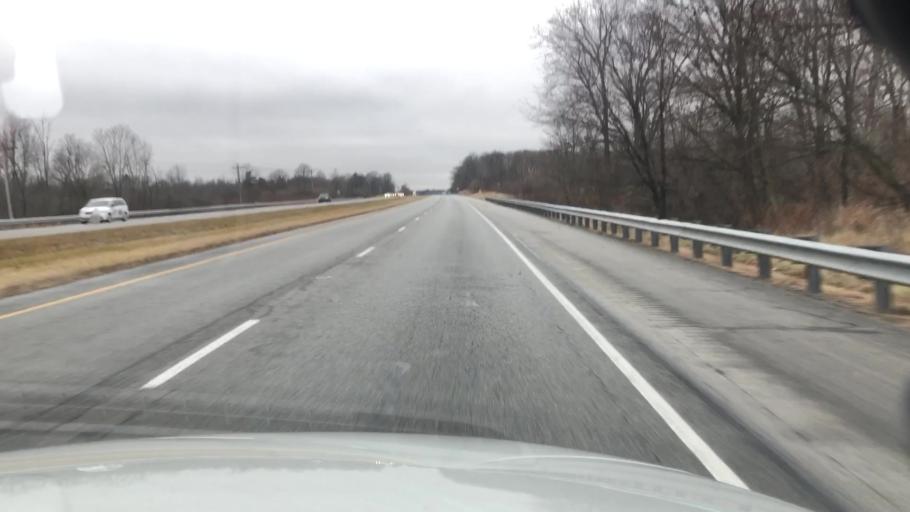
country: US
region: Indiana
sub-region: Whitley County
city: Columbia City
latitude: 41.1777
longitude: -85.5803
